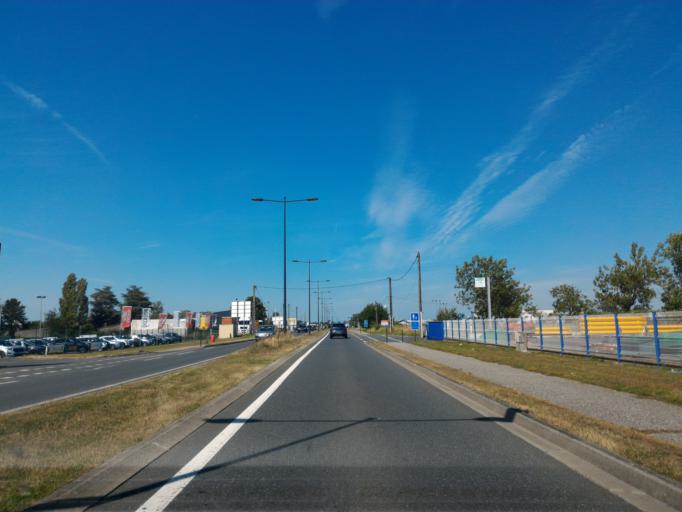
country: FR
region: Centre
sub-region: Departement de l'Indre
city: Saint-Maur
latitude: 46.7856
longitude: 1.6574
